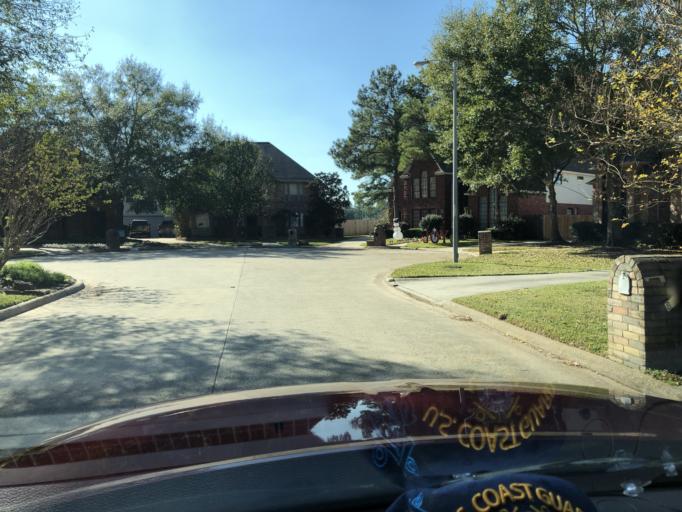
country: US
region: Texas
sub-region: Harris County
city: Tomball
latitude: 30.0321
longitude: -95.5477
